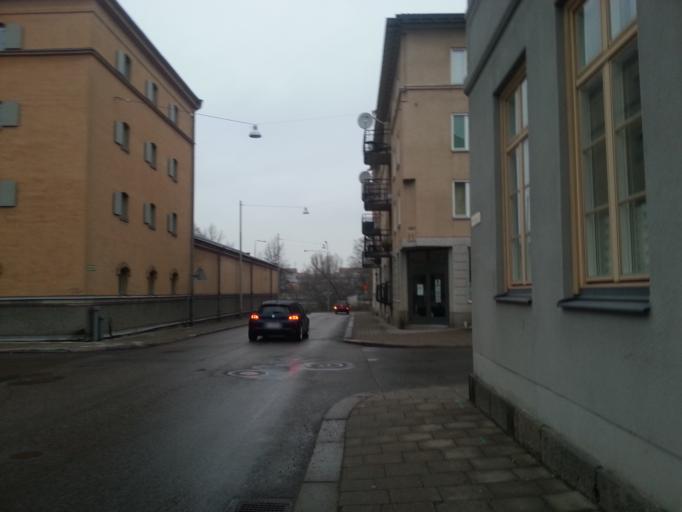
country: SE
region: OEstergoetland
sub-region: Norrkopings Kommun
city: Norrkoping
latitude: 58.5927
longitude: 16.1906
